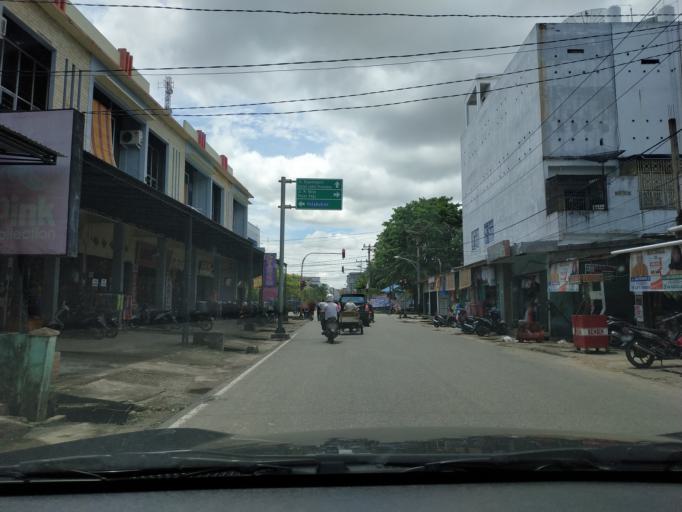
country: ID
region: Riau
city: Tembilahan
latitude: -0.3234
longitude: 103.1590
